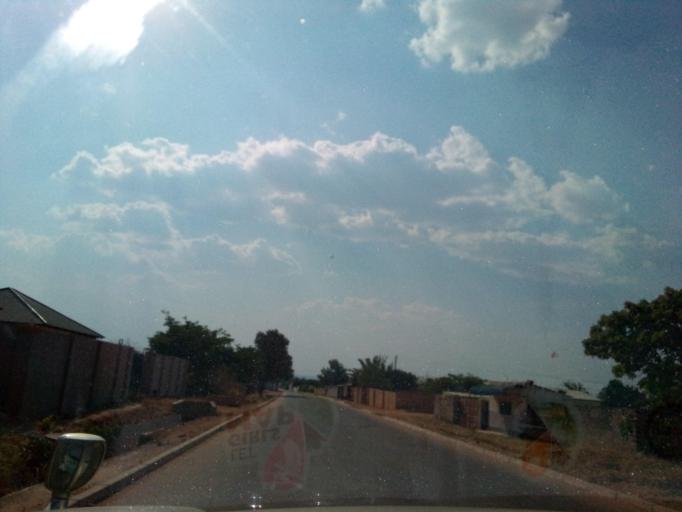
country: ZM
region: Northern
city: Mpika
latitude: -11.8460
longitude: 31.4488
